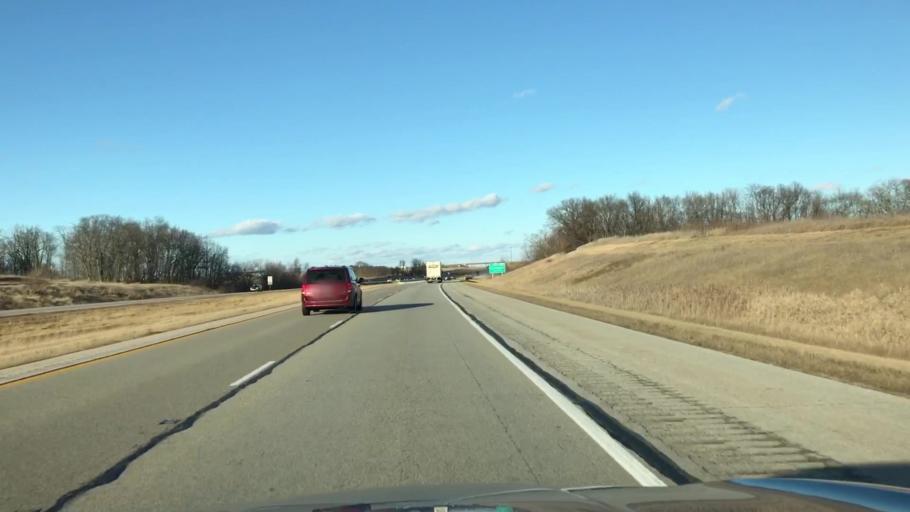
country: US
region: Illinois
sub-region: McLean County
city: Lexington
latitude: 40.6328
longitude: -88.8151
